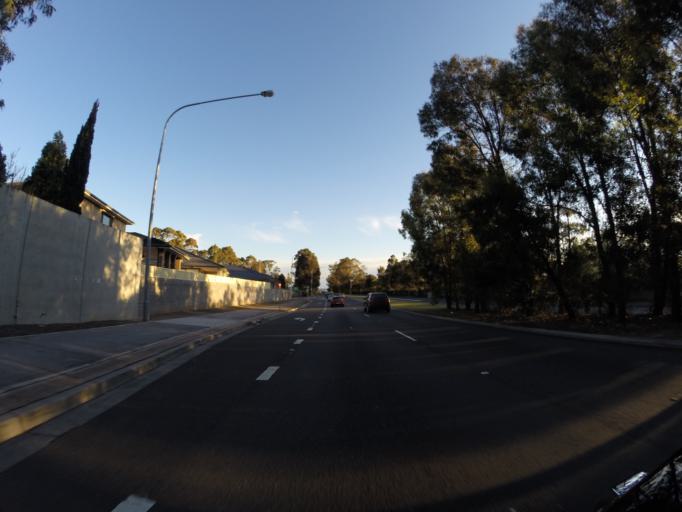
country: AU
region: New South Wales
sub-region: Fairfield
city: Cecil Park
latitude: -33.8856
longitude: 150.8632
